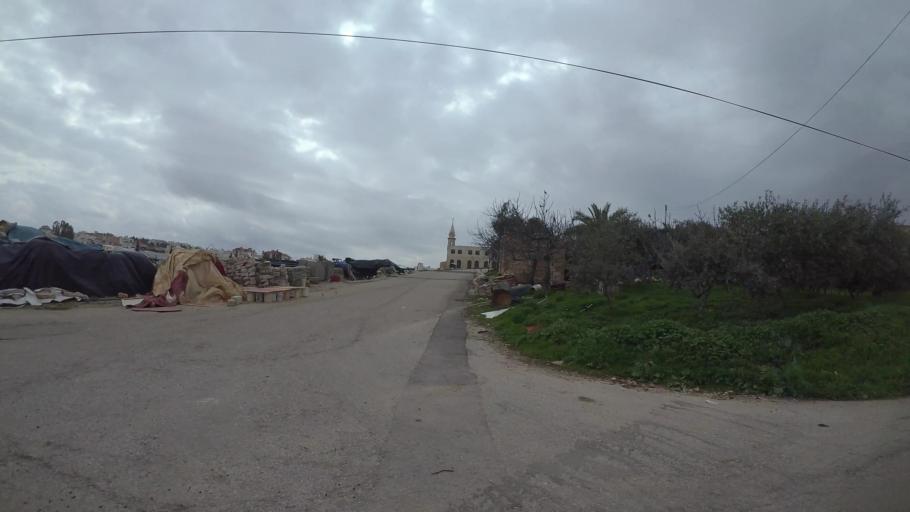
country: JO
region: Amman
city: Wadi as Sir
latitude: 31.9297
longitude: 35.8575
